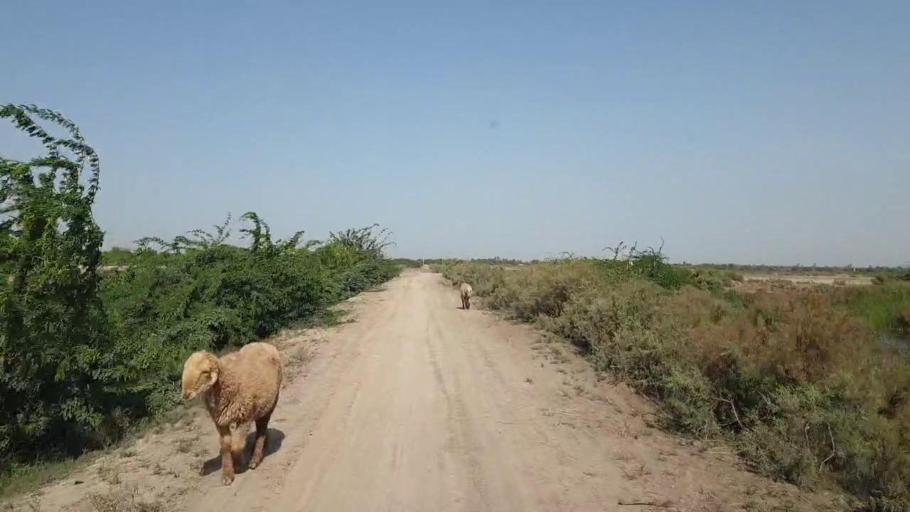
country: PK
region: Sindh
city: Tando Bago
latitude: 24.6593
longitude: 69.0693
